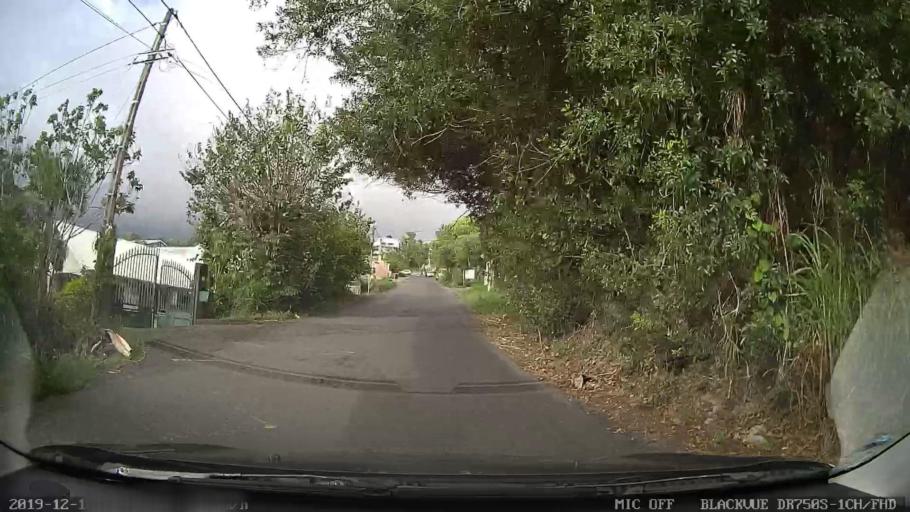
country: RE
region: Reunion
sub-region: Reunion
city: Le Tampon
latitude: -21.2569
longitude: 55.5159
